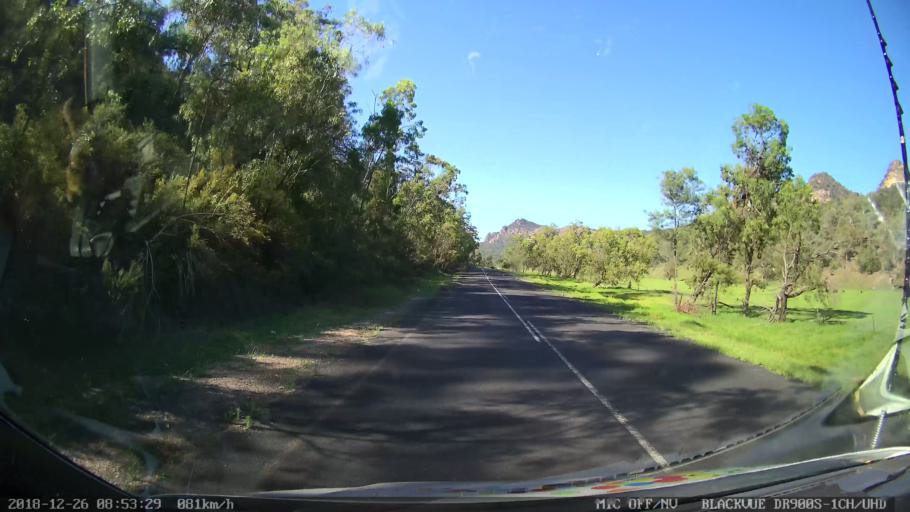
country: AU
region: New South Wales
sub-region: Mid-Western Regional
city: Kandos
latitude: -32.6046
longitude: 150.0772
